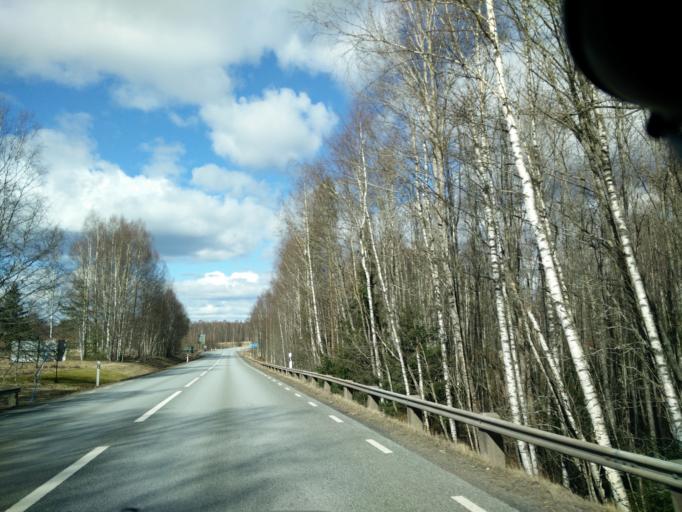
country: SE
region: Vaermland
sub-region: Munkfors Kommun
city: Munkfors
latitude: 59.8587
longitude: 13.5619
